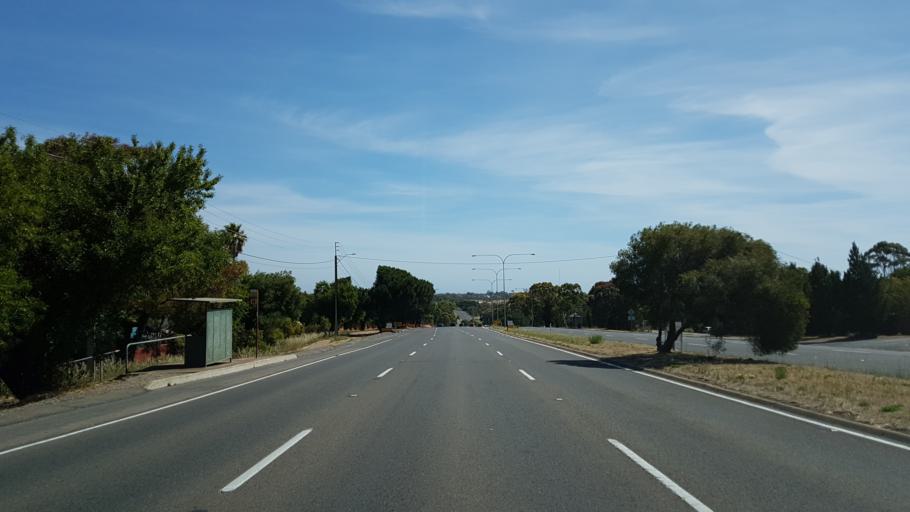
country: AU
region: South Australia
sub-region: Marion
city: Trott Park
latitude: -35.0735
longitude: 138.5522
